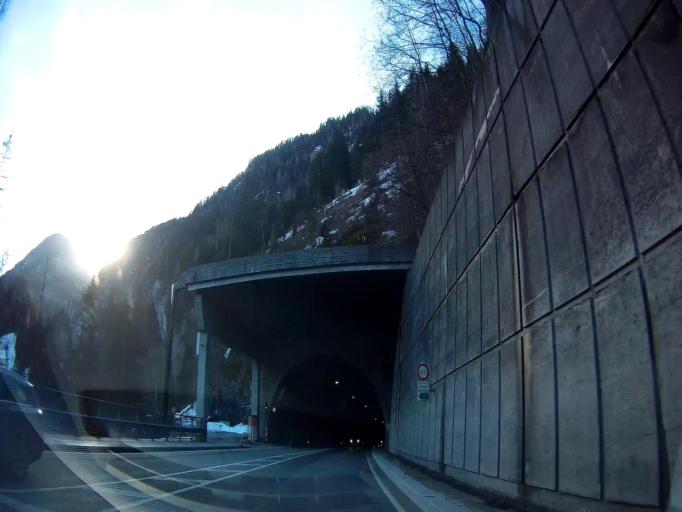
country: AT
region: Salzburg
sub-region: Politischer Bezirk Zell am See
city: Lend
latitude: 47.2901
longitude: 13.0598
